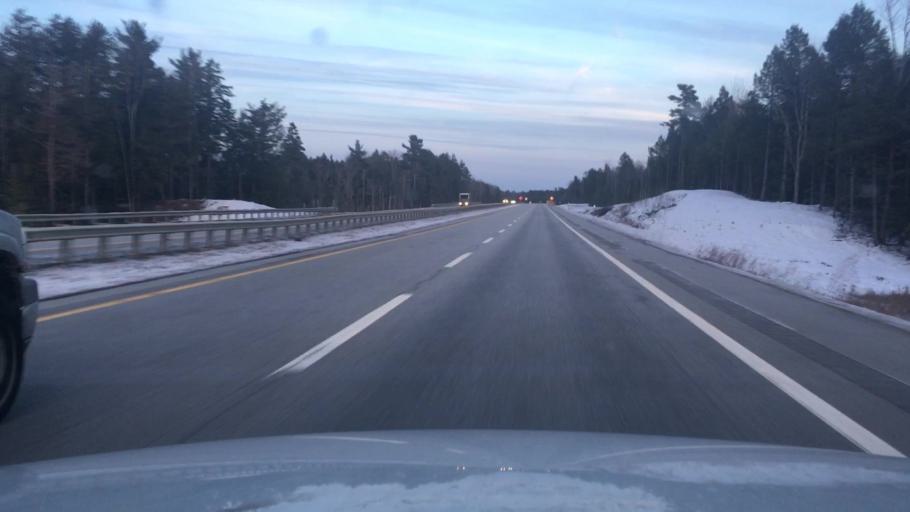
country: US
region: Maine
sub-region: Sagadahoc County
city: Richmond
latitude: 44.1620
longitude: -69.8853
